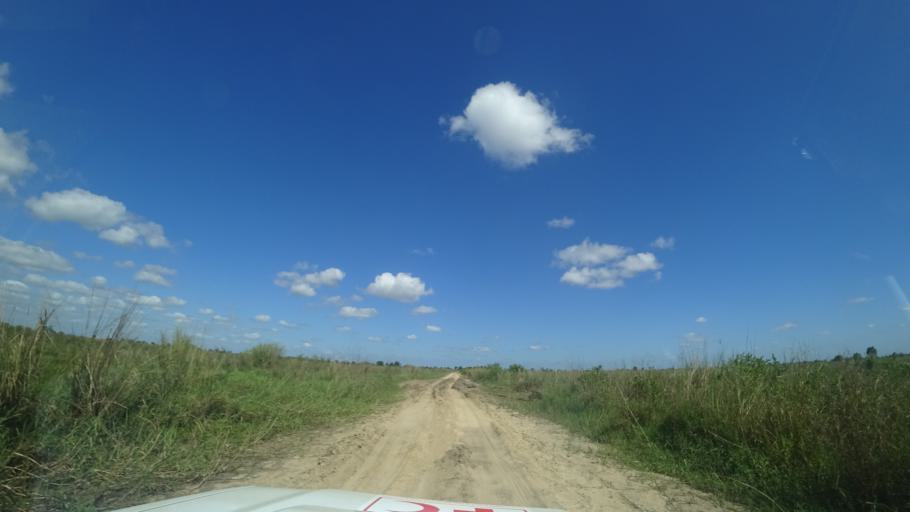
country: MZ
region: Sofala
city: Dondo
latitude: -19.3971
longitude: 34.5713
